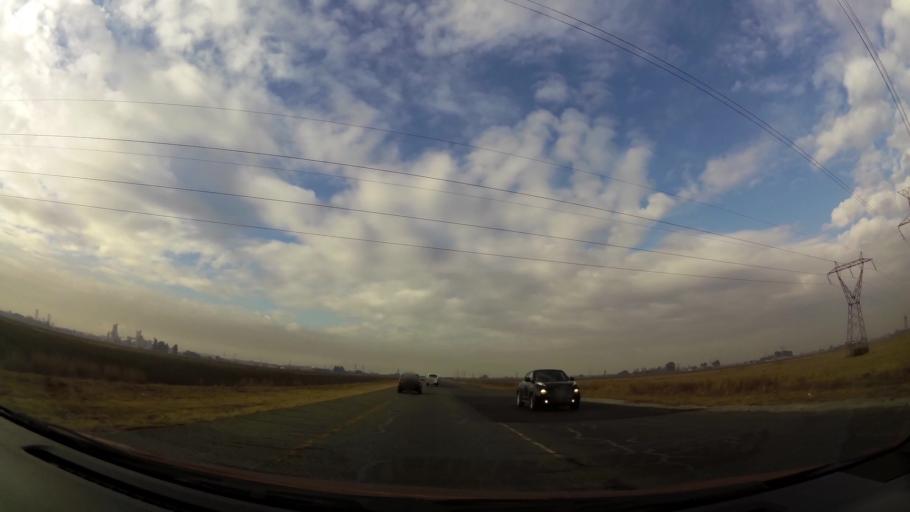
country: ZA
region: Gauteng
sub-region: Sedibeng District Municipality
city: Vanderbijlpark
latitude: -26.6664
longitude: 27.7876
